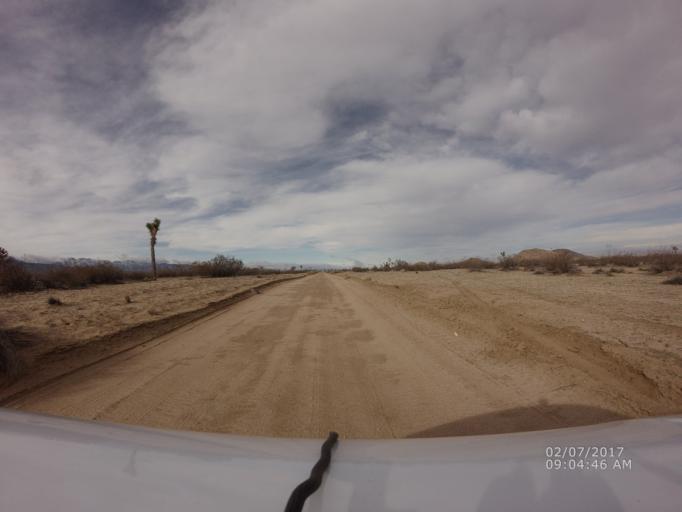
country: US
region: California
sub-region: San Bernardino County
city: Pinon Hills
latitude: 34.5276
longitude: -117.6873
